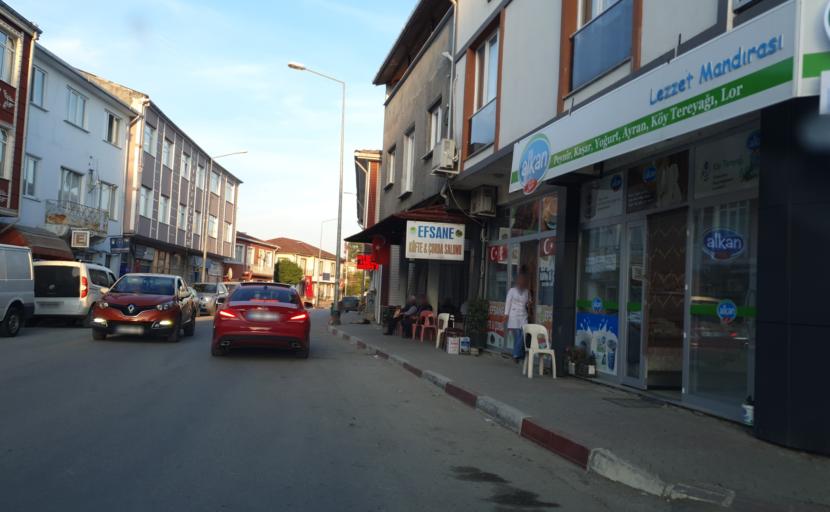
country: TR
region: Kirklareli
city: Sergen
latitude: 41.8250
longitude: 27.7672
